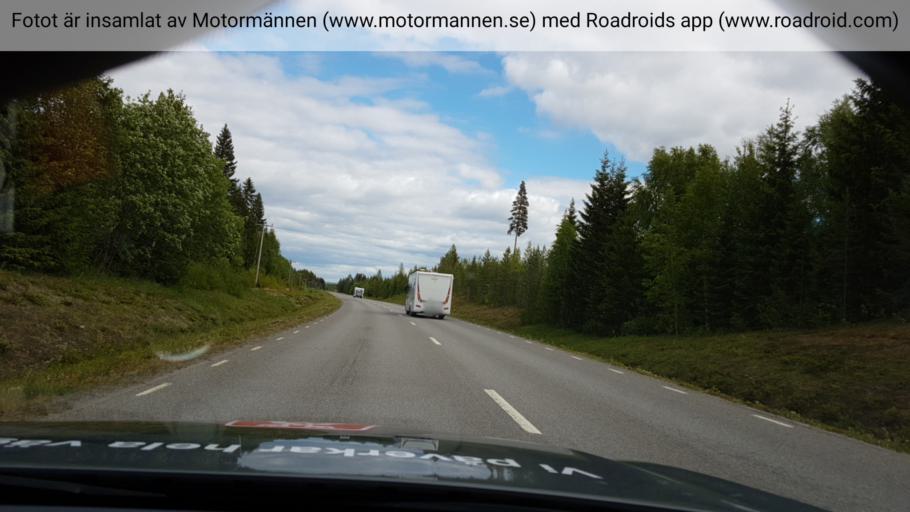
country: SE
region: Jaemtland
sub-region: Stroemsunds Kommun
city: Stroemsund
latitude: 64.2342
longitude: 15.4653
